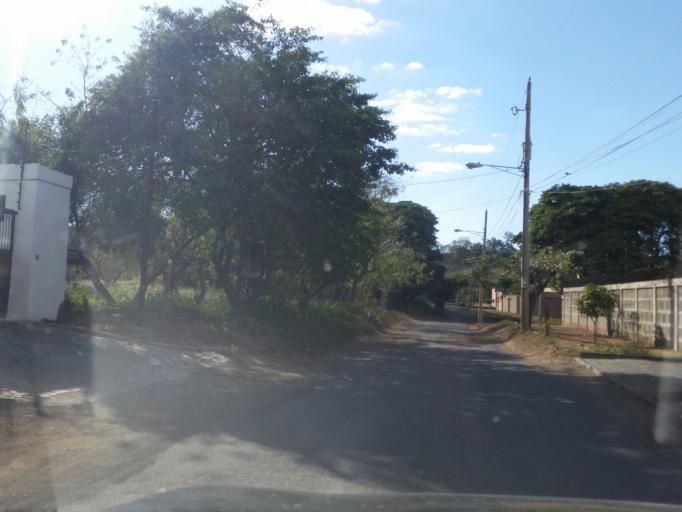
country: NI
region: Managua
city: Managua
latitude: 12.0779
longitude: -86.2494
